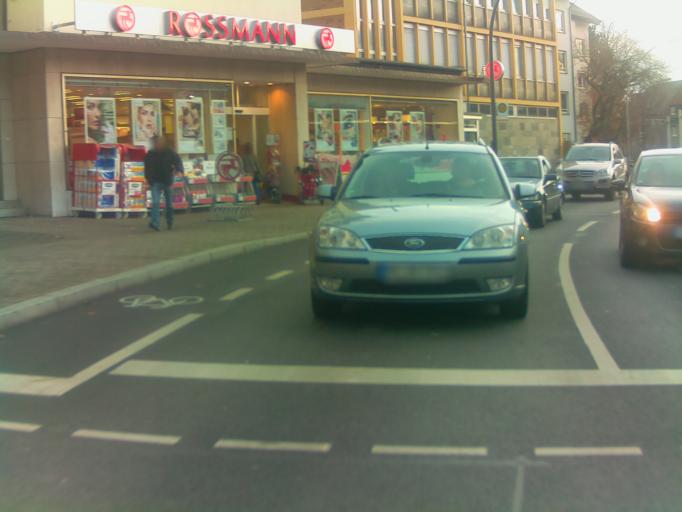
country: DE
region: Baden-Wuerttemberg
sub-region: Karlsruhe Region
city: Heidelberg
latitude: 49.4282
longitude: 8.6833
